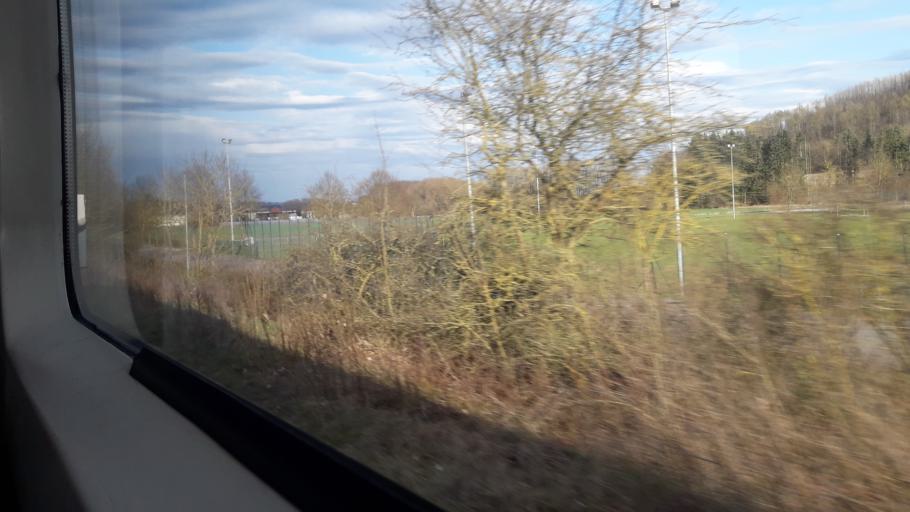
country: DE
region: North Rhine-Westphalia
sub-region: Regierungsbezirk Detmold
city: Willebadessen
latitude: 51.5217
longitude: 9.0181
